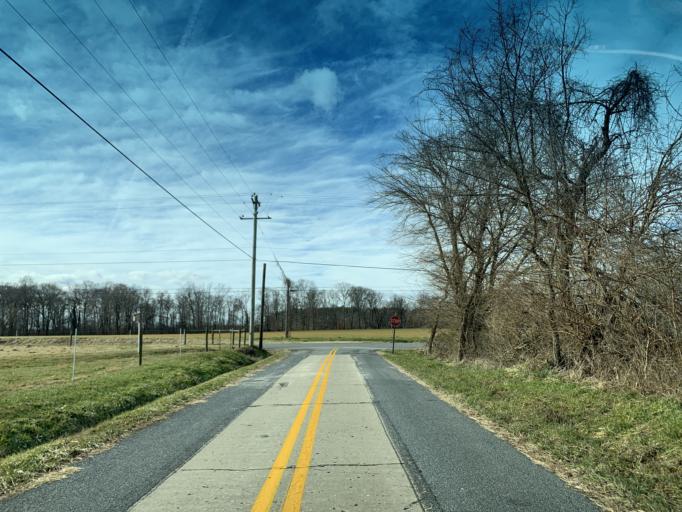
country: US
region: Maryland
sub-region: Harford County
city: Aberdeen Proving Ground
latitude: 39.3493
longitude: -76.0611
